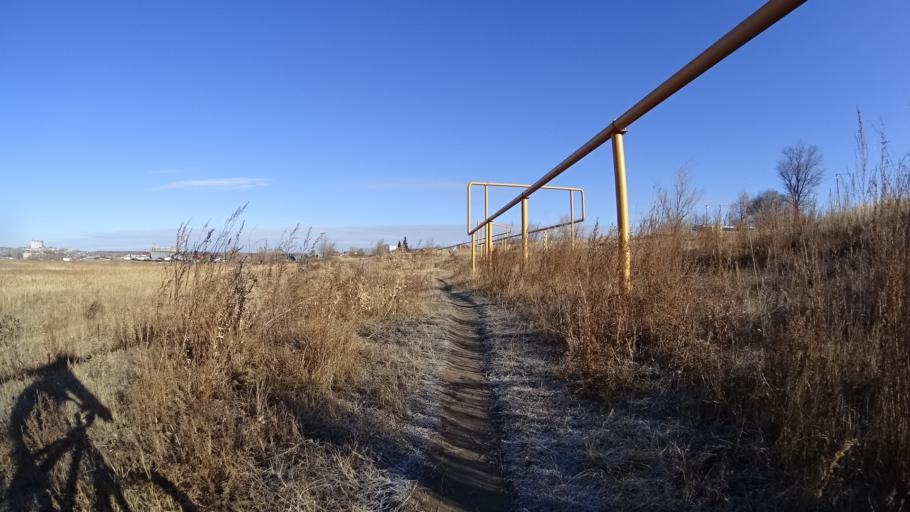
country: RU
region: Chelyabinsk
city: Troitsk
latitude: 54.0827
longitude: 61.5923
